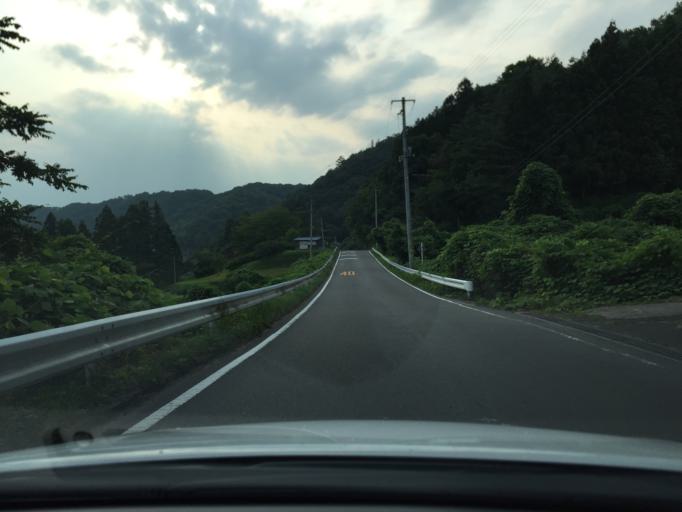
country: JP
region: Fukushima
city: Fukushima-shi
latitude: 37.7205
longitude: 140.4937
